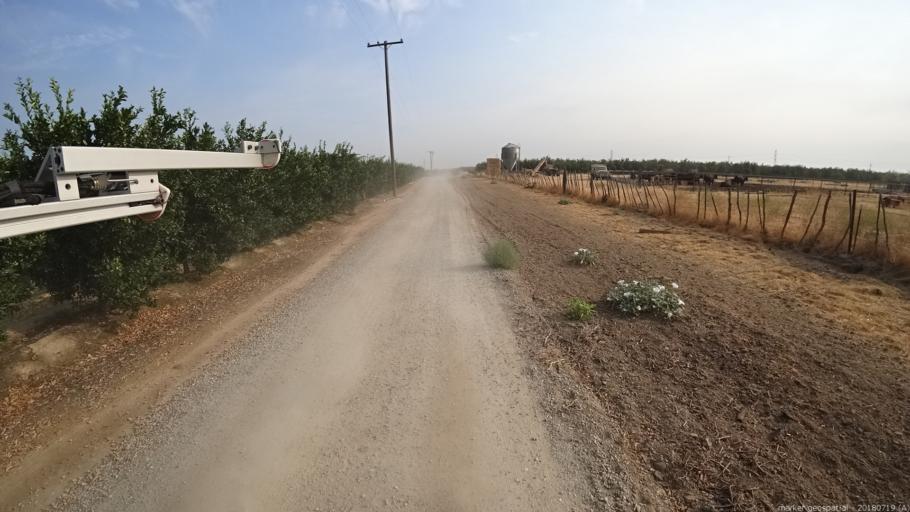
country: US
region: California
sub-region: Madera County
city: Fairmead
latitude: 37.1081
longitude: -120.1932
